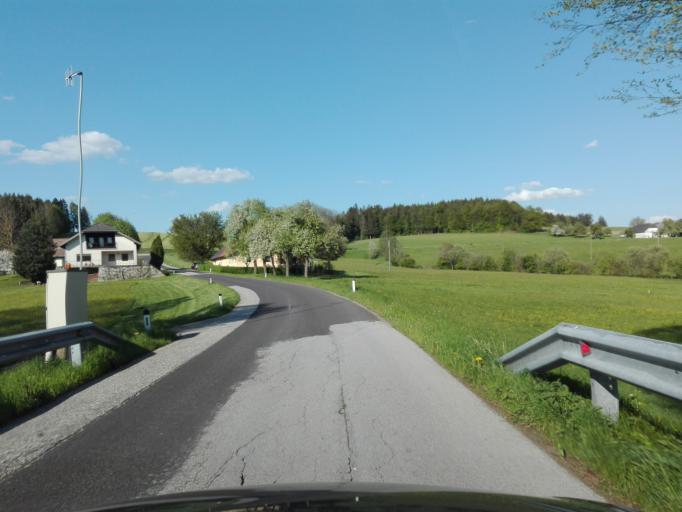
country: AT
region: Upper Austria
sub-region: Politischer Bezirk Rohrbach
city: Pfarrkirchen im Muehlkreis
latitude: 48.4652
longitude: 13.8287
